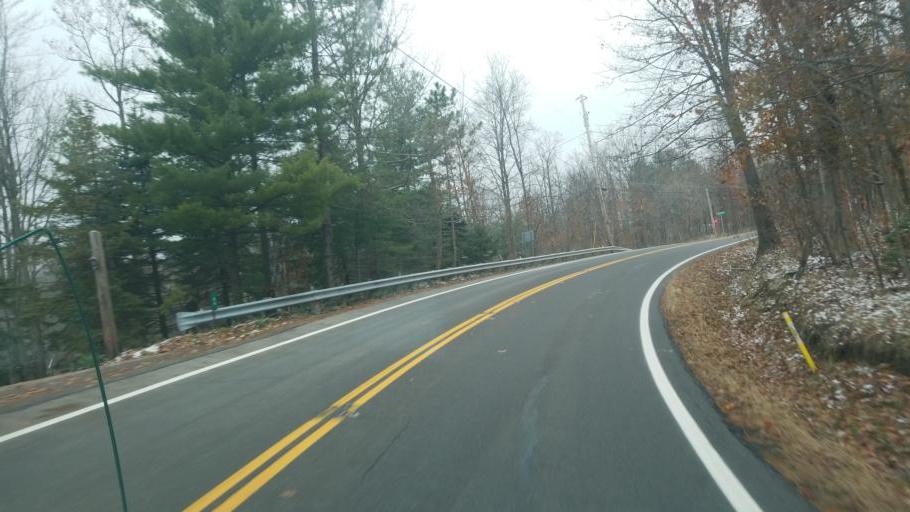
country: US
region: Ohio
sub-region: Cuyahoga County
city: North Royalton
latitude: 41.2743
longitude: -81.7250
